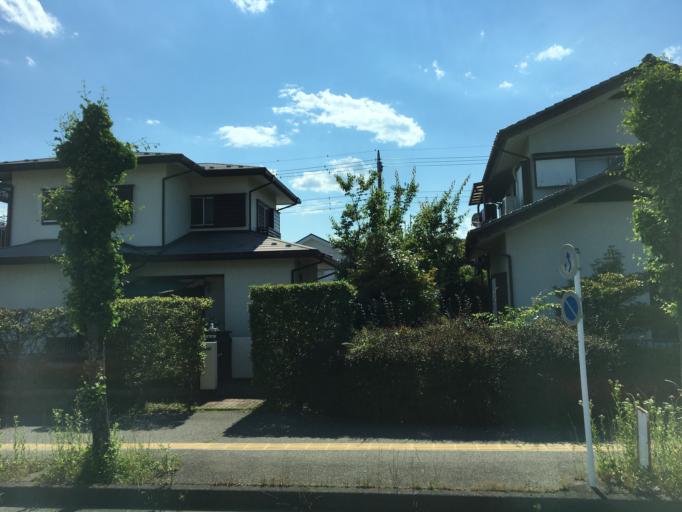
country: JP
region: Saitama
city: Sakado
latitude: 35.9904
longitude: 139.3543
